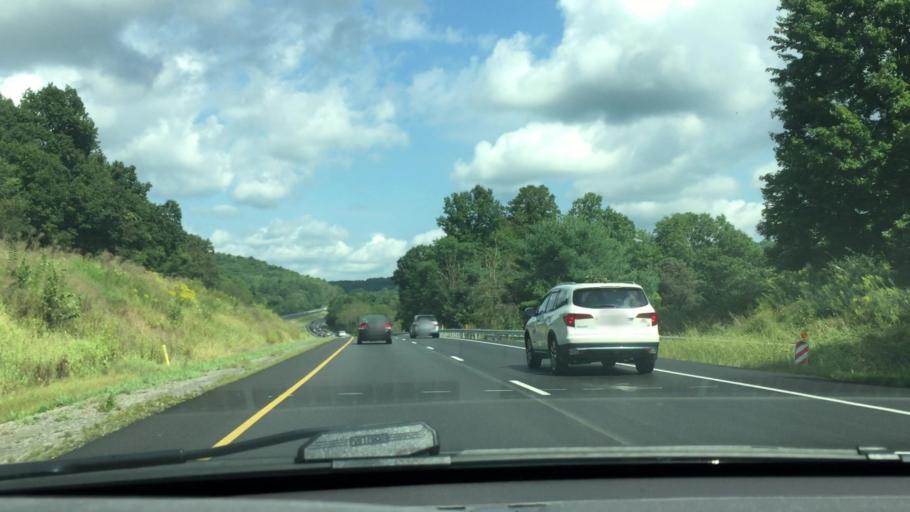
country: US
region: Pennsylvania
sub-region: Butler County
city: Prospect
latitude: 40.8672
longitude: -80.1113
